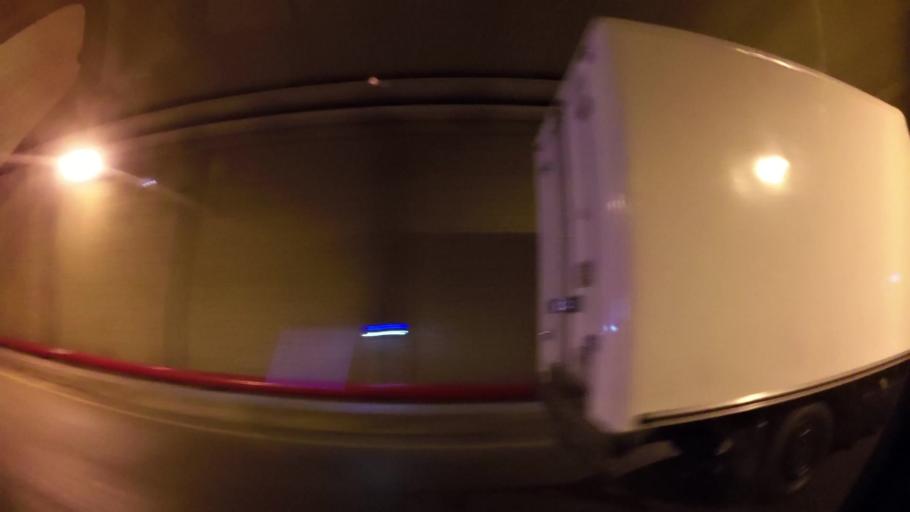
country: CO
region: Bolivar
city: Cartagena
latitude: 10.4484
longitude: -75.5203
